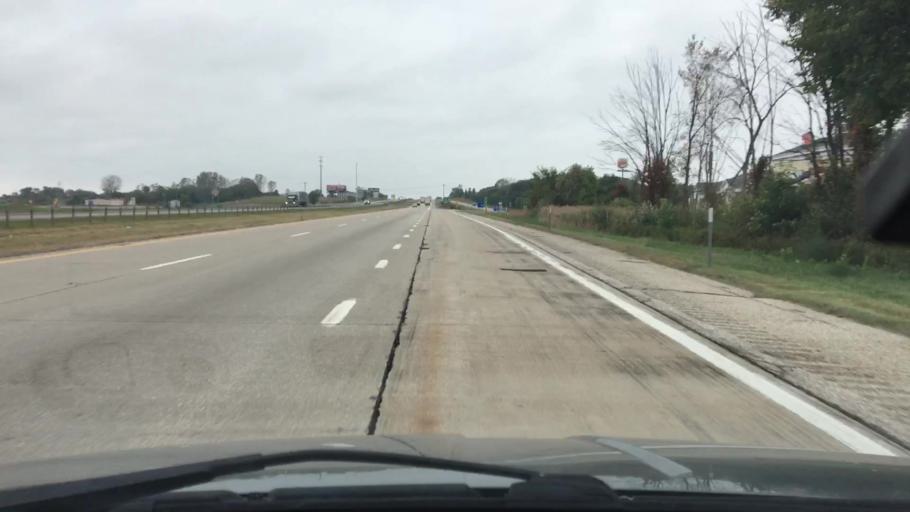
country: US
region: Michigan
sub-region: Berrien County
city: Watervliet
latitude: 42.1787
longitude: -86.2557
